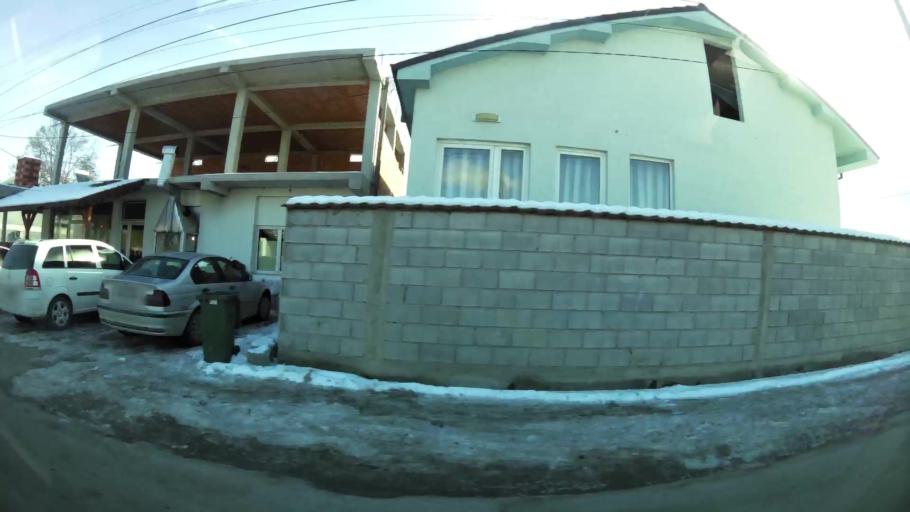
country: MK
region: Saraj
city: Saraj
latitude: 41.9942
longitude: 21.3270
